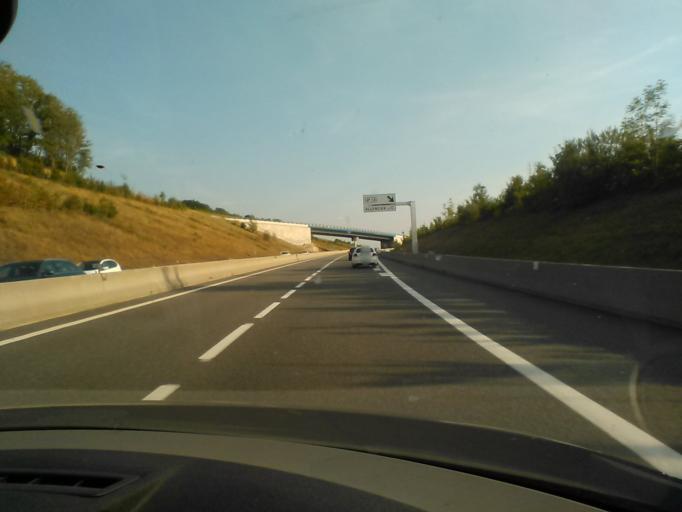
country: FR
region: Rhone-Alpes
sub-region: Departement de la Haute-Savoie
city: Allonzier-la-Caille
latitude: 46.0047
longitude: 6.1264
